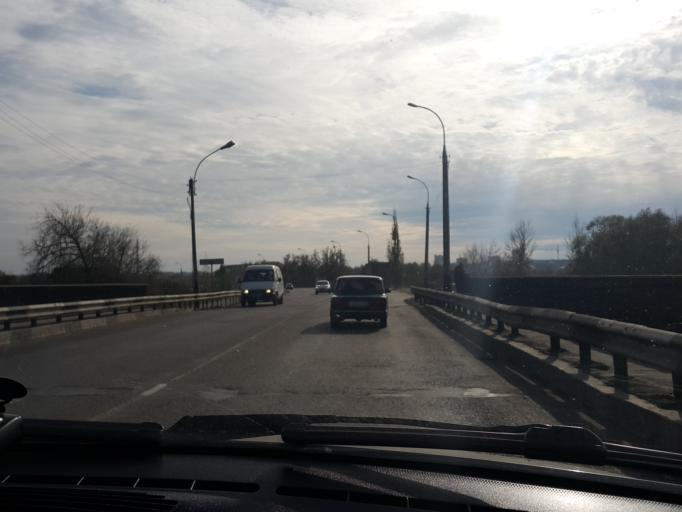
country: RU
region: Tambov
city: Tambov
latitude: 52.7270
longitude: 41.4649
